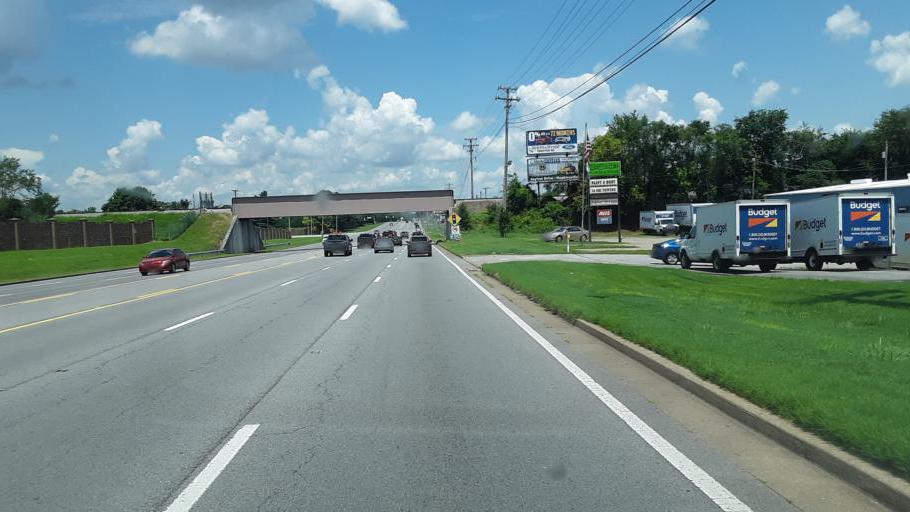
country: US
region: Kentucky
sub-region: Christian County
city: Fort Campbell North
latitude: 36.6190
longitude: -87.4311
